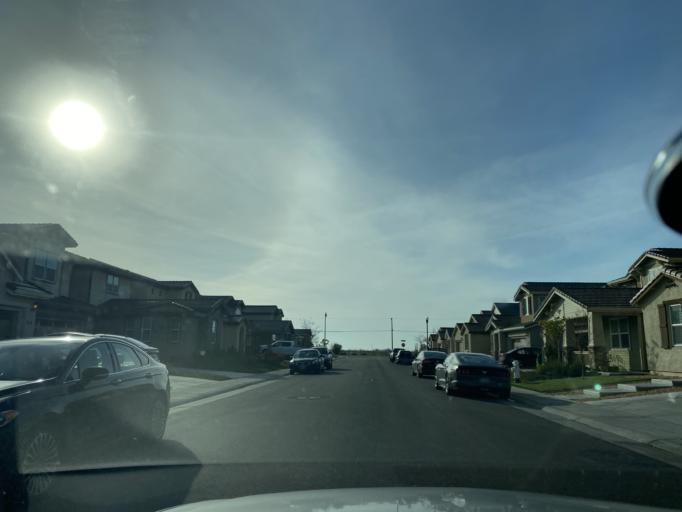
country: US
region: California
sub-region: Sacramento County
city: Elk Grove
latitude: 38.3919
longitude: -121.3965
